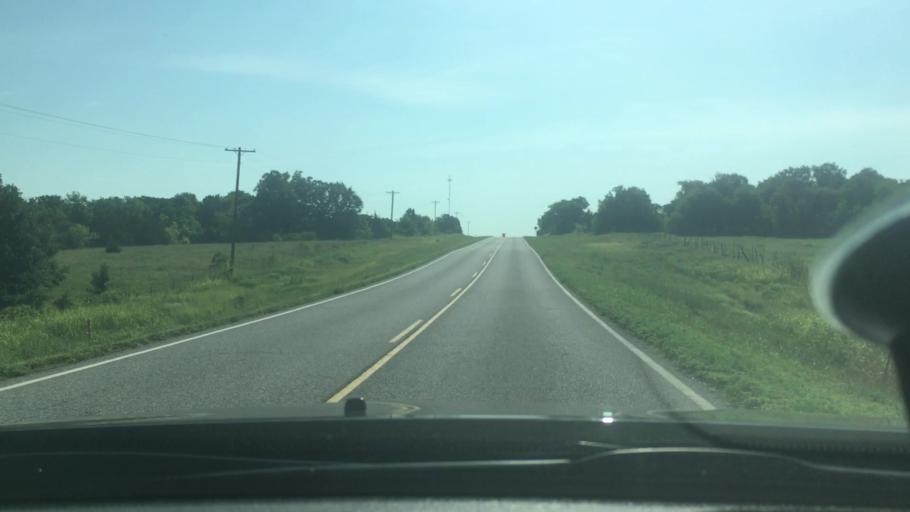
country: US
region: Oklahoma
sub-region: Garvin County
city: Pauls Valley
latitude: 34.6517
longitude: -97.2718
